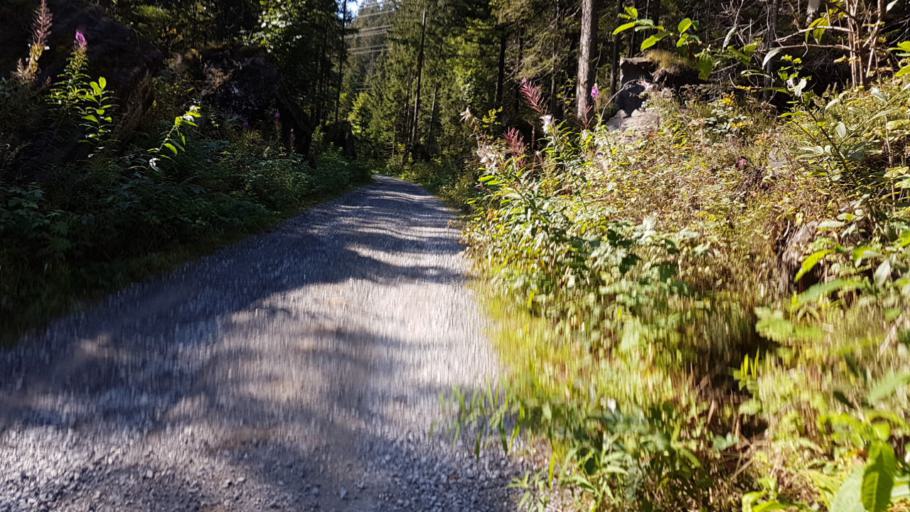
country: CH
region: Bern
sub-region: Frutigen-Niedersimmental District
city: Kandersteg
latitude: 46.5074
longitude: 7.6733
